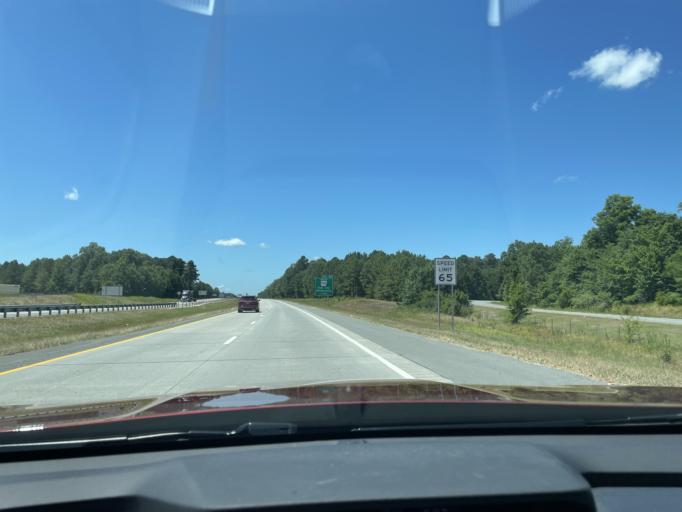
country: US
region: Arkansas
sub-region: Jefferson County
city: Pine Bluff
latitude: 34.1935
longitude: -91.9777
